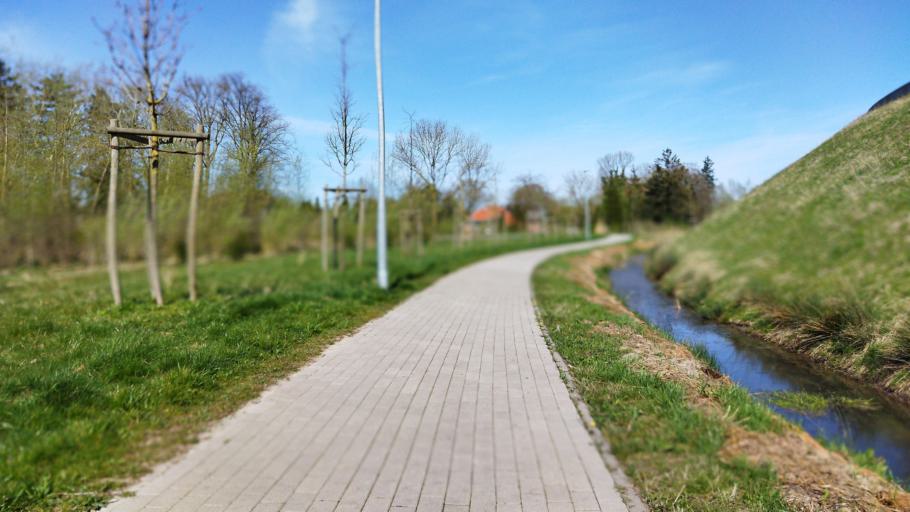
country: DE
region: Lower Saxony
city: Brake (Unterweser)
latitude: 53.3440
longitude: 8.4806
